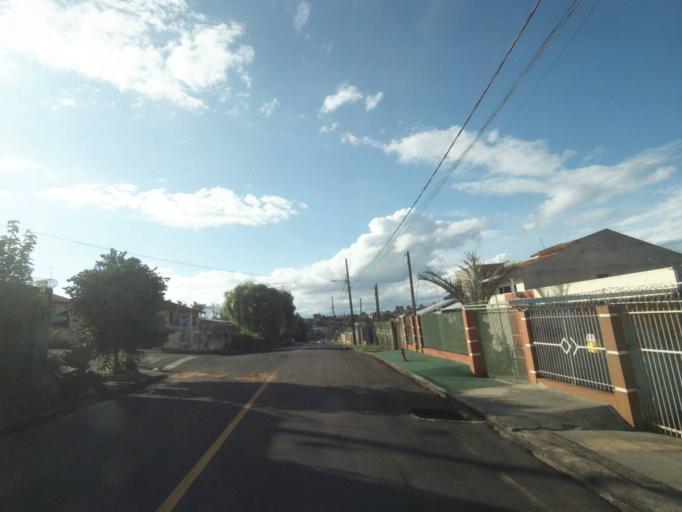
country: BR
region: Parana
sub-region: Telemaco Borba
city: Telemaco Borba
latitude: -24.3404
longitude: -50.6186
